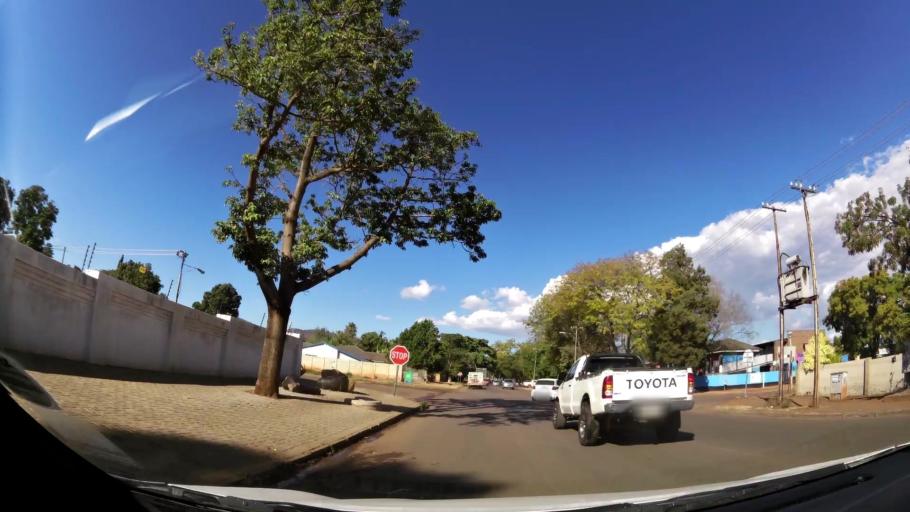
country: ZA
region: Limpopo
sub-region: Waterberg District Municipality
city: Mokopane
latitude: -24.1775
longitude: 29.0126
